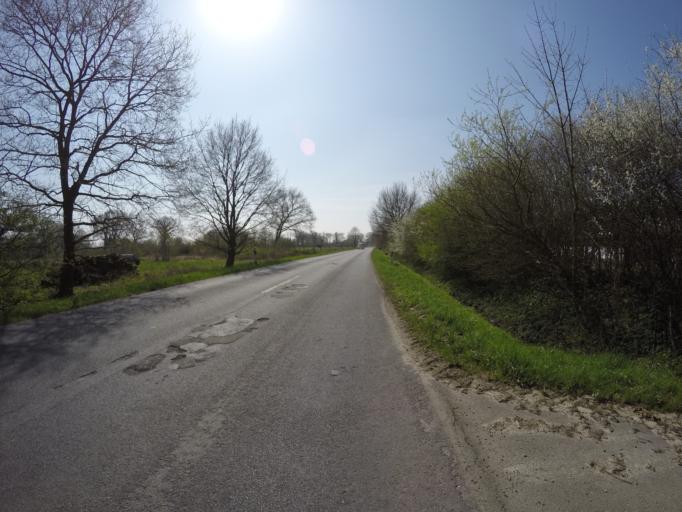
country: DE
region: Schleswig-Holstein
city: Quickborn
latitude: 53.7186
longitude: 9.8859
